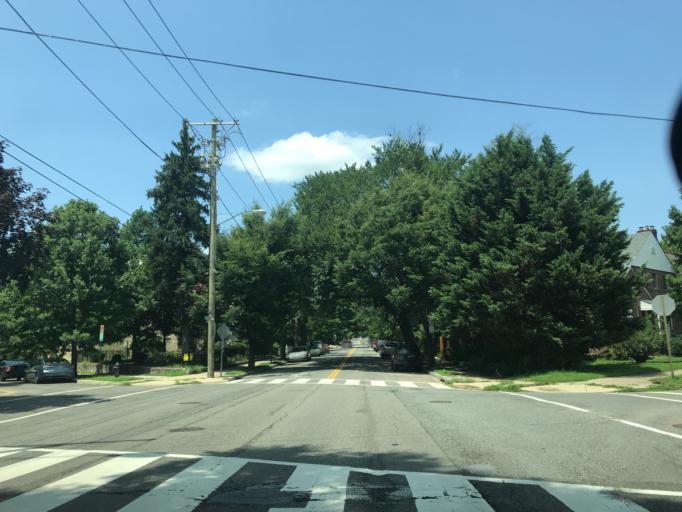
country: US
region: Maryland
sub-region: Montgomery County
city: Friendship Village
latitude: 38.9519
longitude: -77.0848
